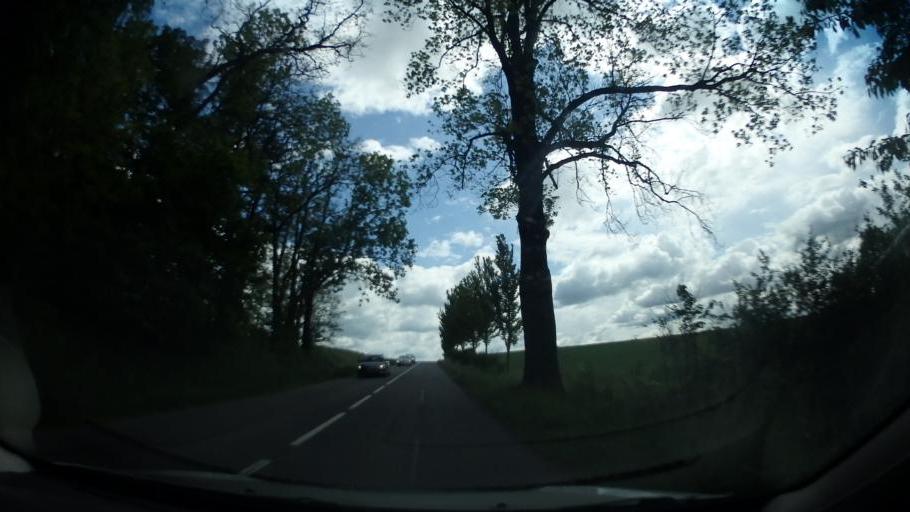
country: CZ
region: Pardubicky
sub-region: Okres Svitavy
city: Moravska Trebova
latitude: 49.7246
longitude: 16.6408
